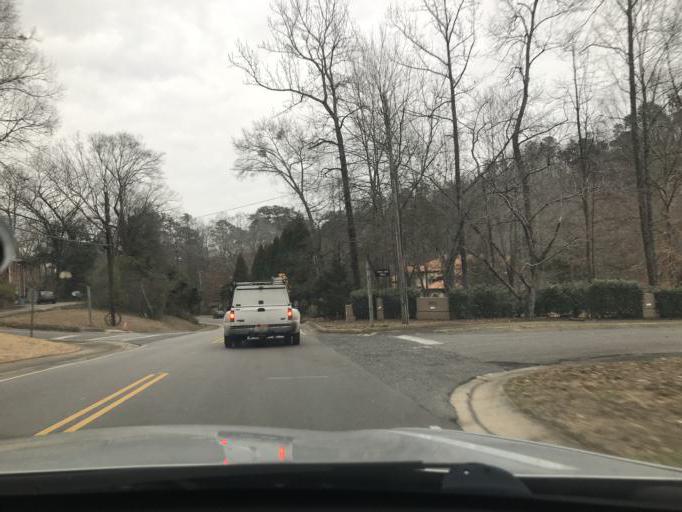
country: US
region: Alabama
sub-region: Jefferson County
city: Cahaba Heights
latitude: 33.4793
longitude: -86.7153
